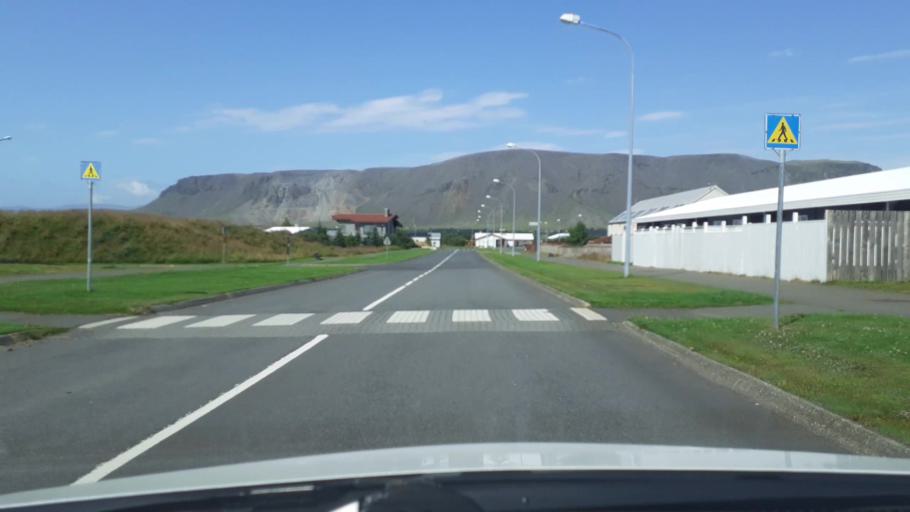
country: IS
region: South
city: Selfoss
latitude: 63.9321
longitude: -21.0192
